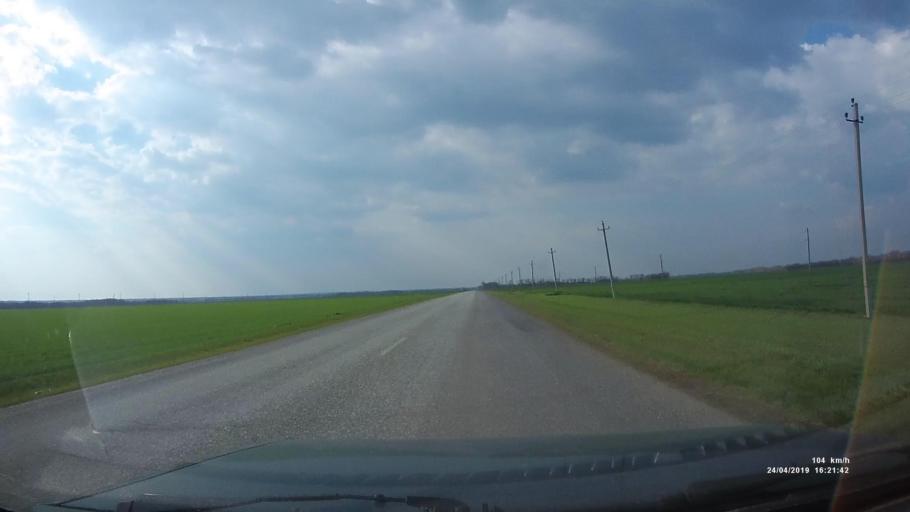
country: RU
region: Rostov
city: Orlovskiy
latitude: 46.8089
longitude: 42.0628
